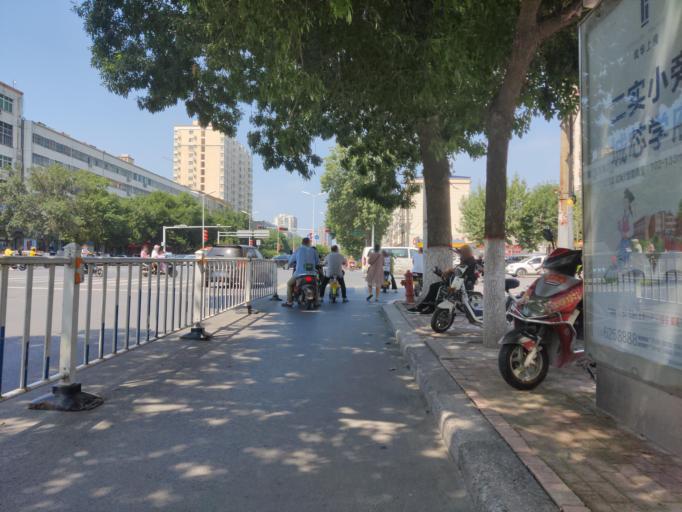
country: CN
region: Henan Sheng
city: Puyang
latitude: 35.7726
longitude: 115.0264
